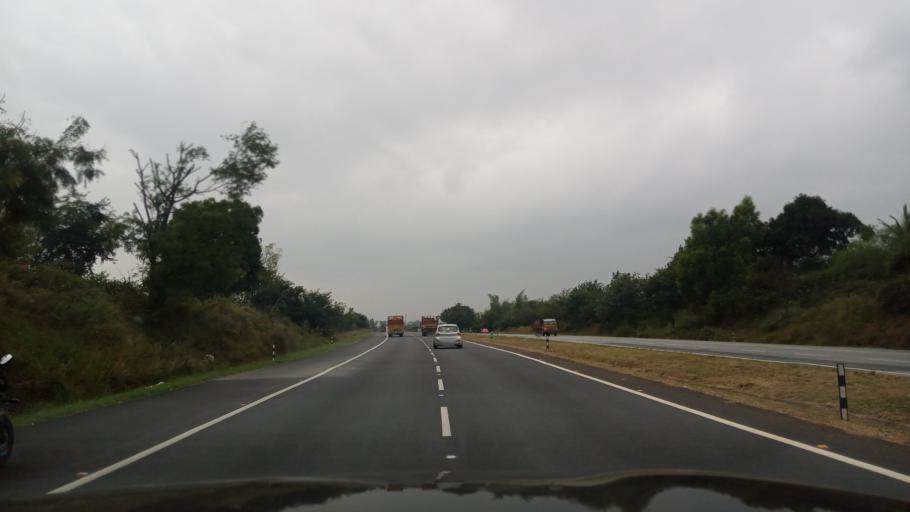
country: IN
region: Karnataka
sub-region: Bangalore Rural
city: Nelamangala
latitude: 13.0071
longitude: 77.4747
